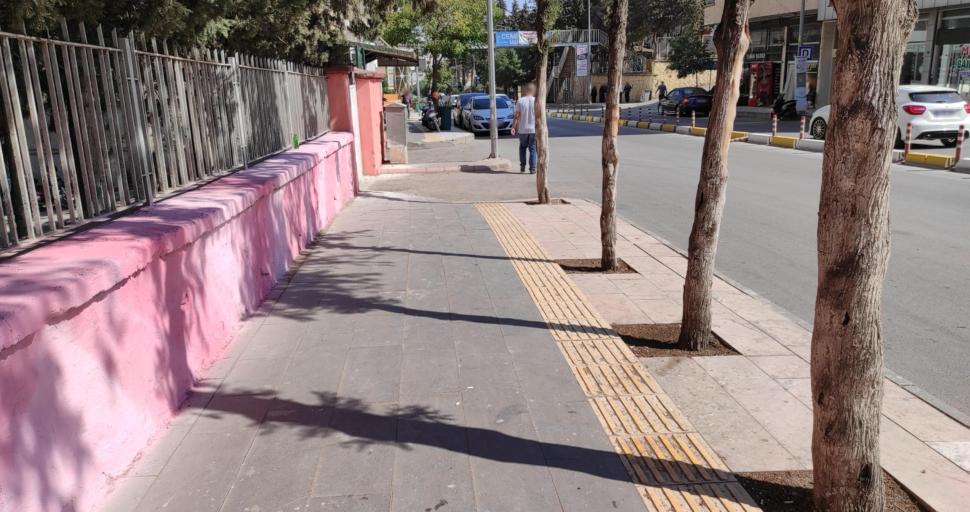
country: TR
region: Kilis
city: Kilis
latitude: 36.7221
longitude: 37.1066
